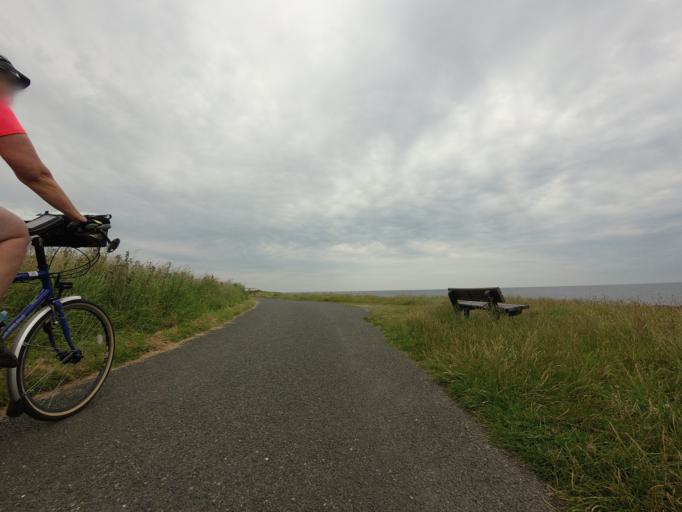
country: GB
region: Scotland
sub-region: Aberdeenshire
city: Whitehills
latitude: 57.6791
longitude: -2.5684
